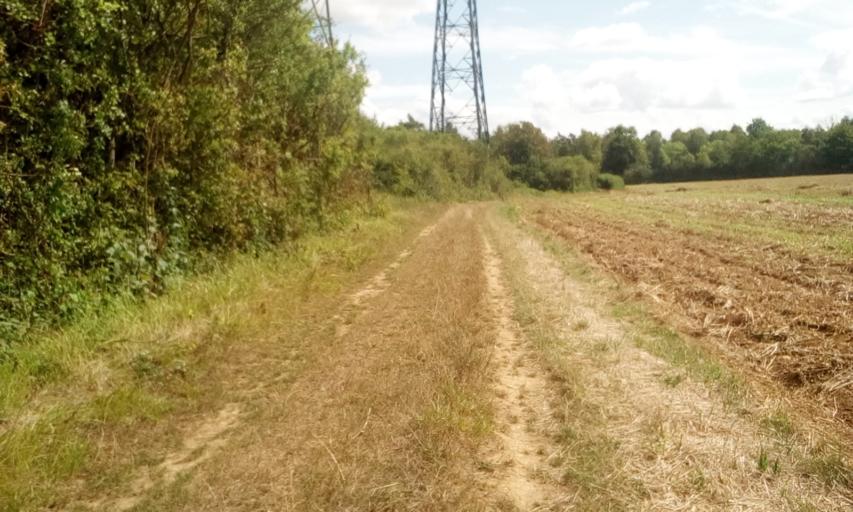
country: FR
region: Lower Normandy
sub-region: Departement du Calvados
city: Cagny
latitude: 49.1102
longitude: -0.2501
